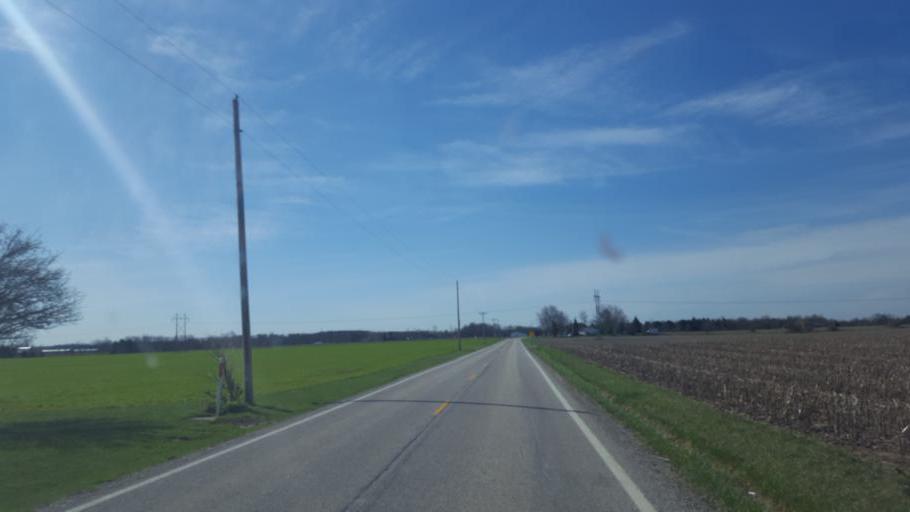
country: US
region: Ohio
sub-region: Morrow County
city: Cardington
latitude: 40.4934
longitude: -82.9632
